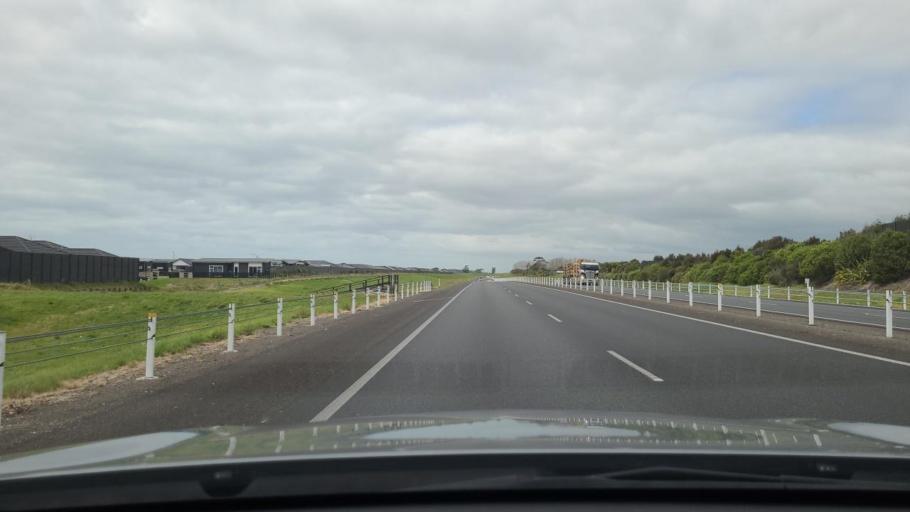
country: NZ
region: Bay of Plenty
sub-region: Western Bay of Plenty District
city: Maketu
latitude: -37.7289
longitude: 176.3338
